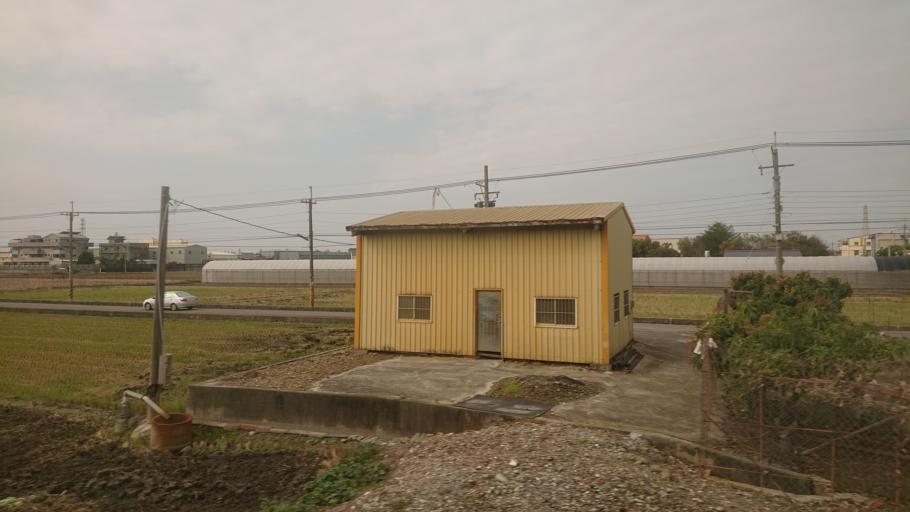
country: TW
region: Taiwan
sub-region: Changhua
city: Chang-hua
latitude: 24.0327
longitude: 120.5337
